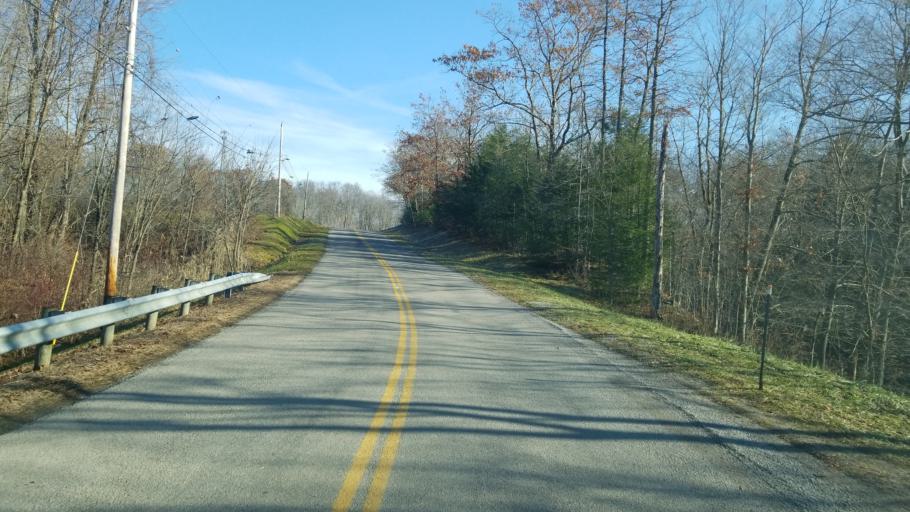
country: US
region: Ohio
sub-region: Ashtabula County
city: Jefferson
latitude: 41.7375
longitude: -80.7302
